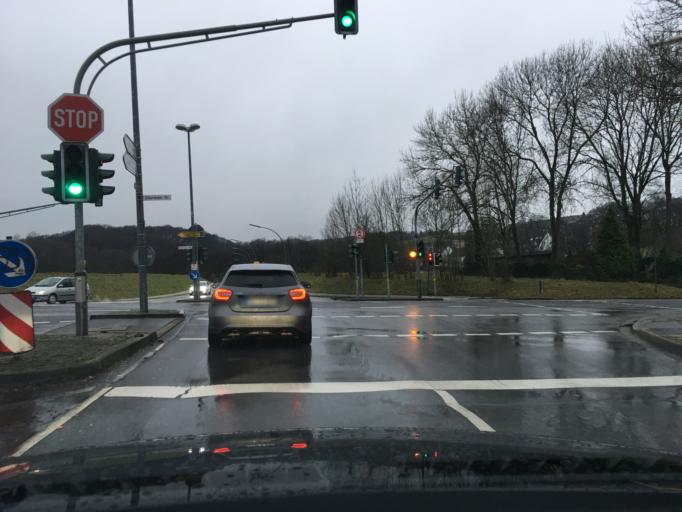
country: DE
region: North Rhine-Westphalia
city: Wulfrath
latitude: 51.2970
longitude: 7.0964
